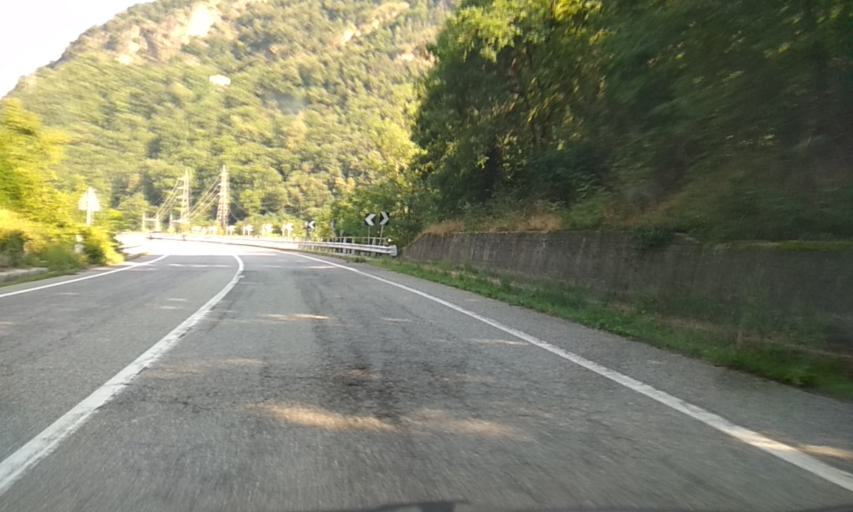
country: IT
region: Piedmont
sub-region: Provincia di Torino
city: Pont-Canavese
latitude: 45.4181
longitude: 7.5897
